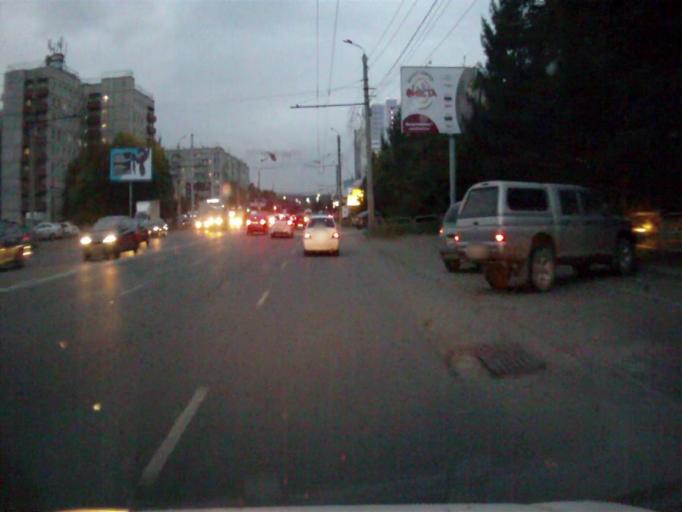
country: RU
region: Chelyabinsk
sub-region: Gorod Chelyabinsk
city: Chelyabinsk
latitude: 55.1808
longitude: 61.3326
